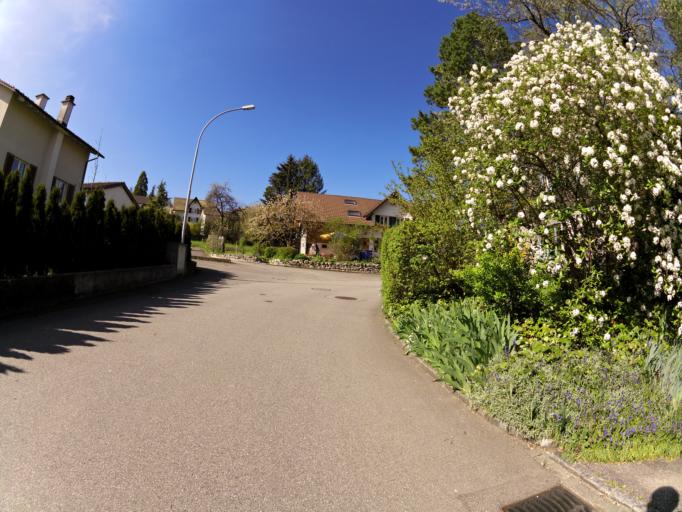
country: CH
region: Solothurn
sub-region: Bezirk Goesgen
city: Niedererlinsbach
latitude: 47.3995
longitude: 8.0060
